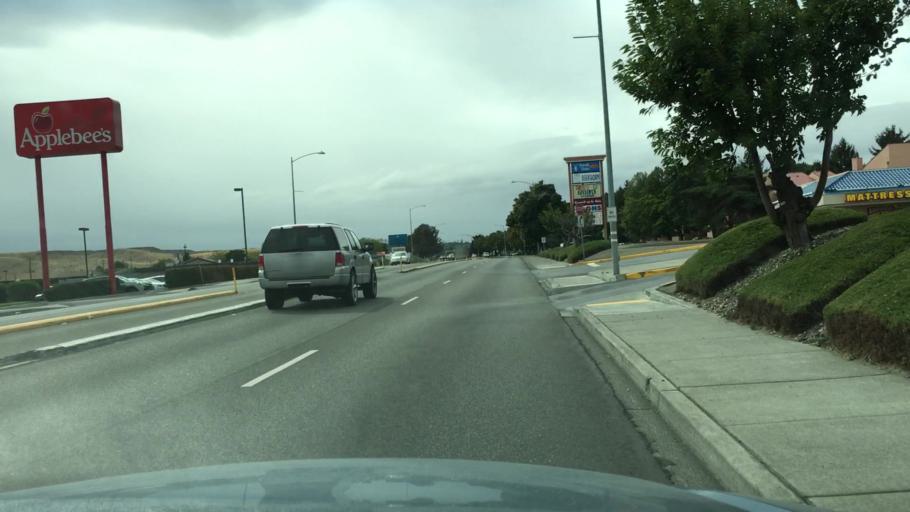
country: US
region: Washington
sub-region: Franklin County
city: West Pasco
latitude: 46.2167
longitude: -119.2250
